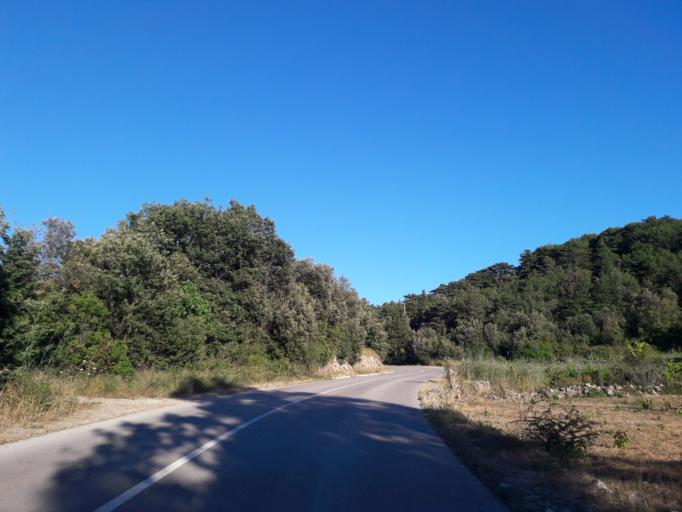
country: HR
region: Dubrovacko-Neretvanska
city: Orebic
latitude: 42.9995
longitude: 17.2573
